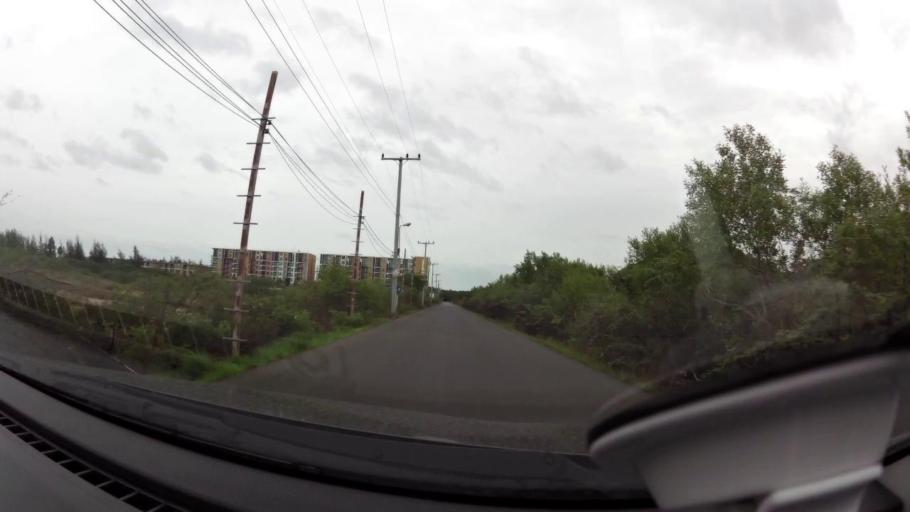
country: TH
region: Prachuap Khiri Khan
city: Pran Buri
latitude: 12.4221
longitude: 99.9797
